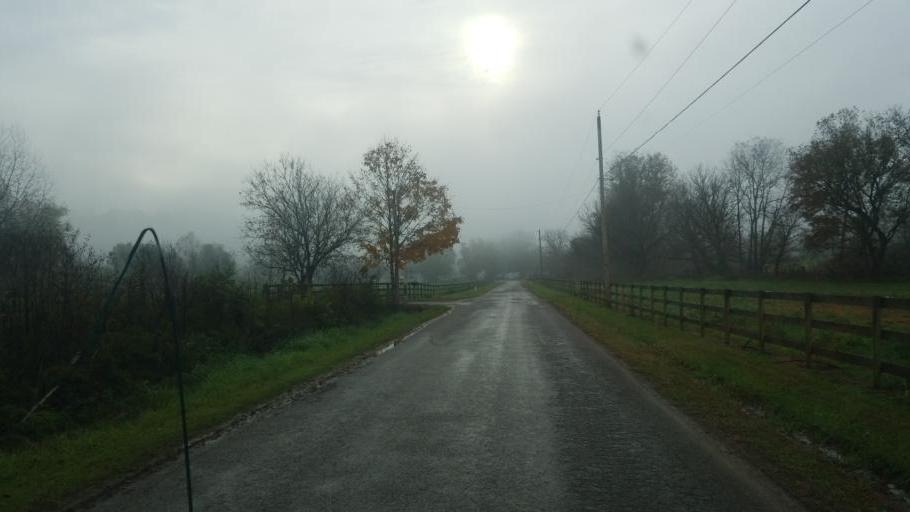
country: US
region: Ohio
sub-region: Athens County
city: Glouster
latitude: 39.4384
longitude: -81.9177
